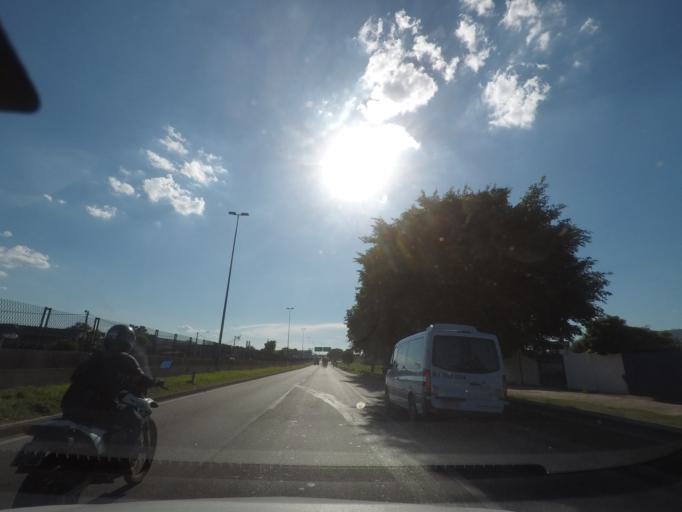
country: BR
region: Rio de Janeiro
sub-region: Duque De Caxias
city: Duque de Caxias
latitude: -22.6696
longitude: -43.2727
